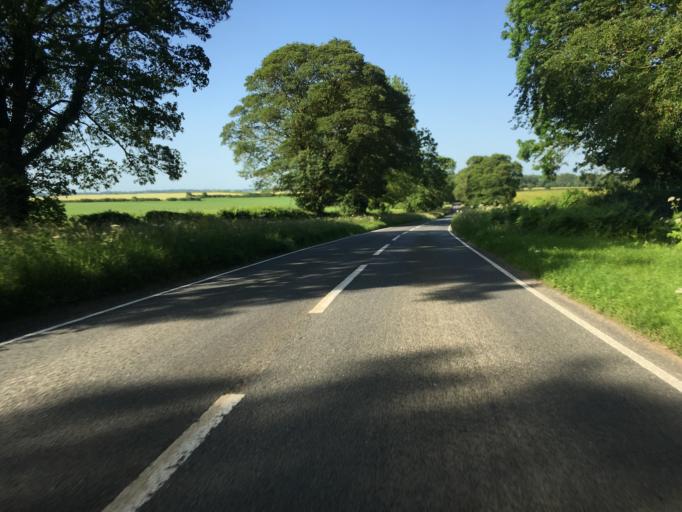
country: GB
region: England
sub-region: Oxfordshire
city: Charlbury
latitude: 51.9046
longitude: -1.4655
